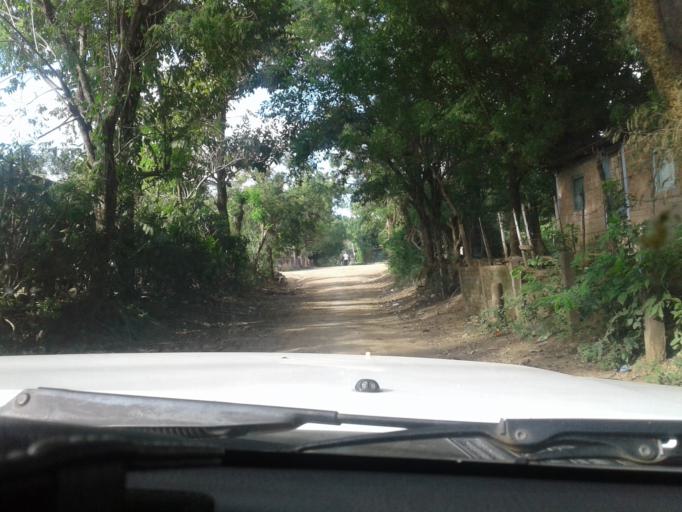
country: NI
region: Rivas
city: Tola
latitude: 11.5208
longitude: -86.0705
